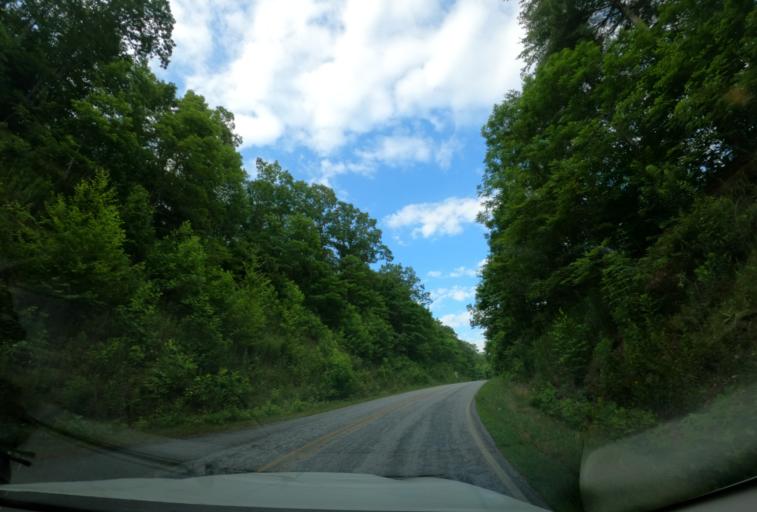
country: US
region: North Carolina
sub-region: Transylvania County
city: Brevard
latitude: 35.1747
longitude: -82.9242
